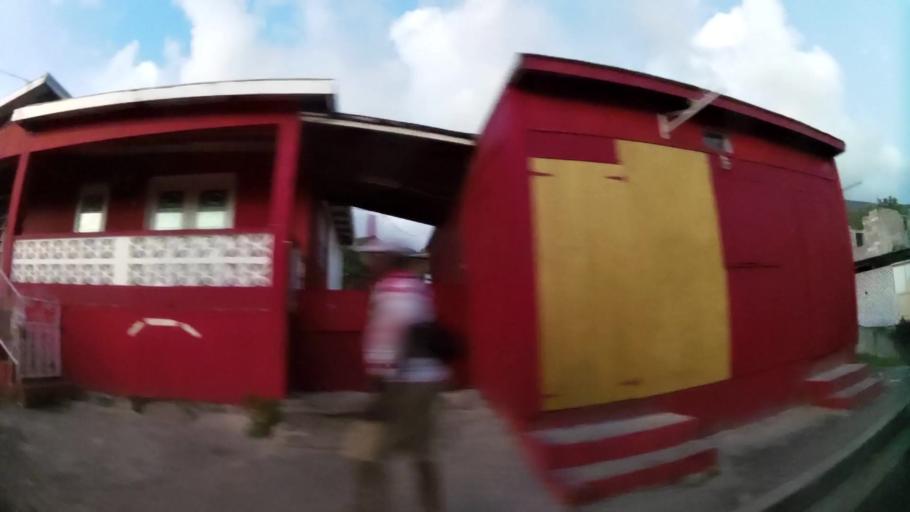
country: KN
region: Saint Thomas Middle Island
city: Middle Island
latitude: 17.3218
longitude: -62.8030
